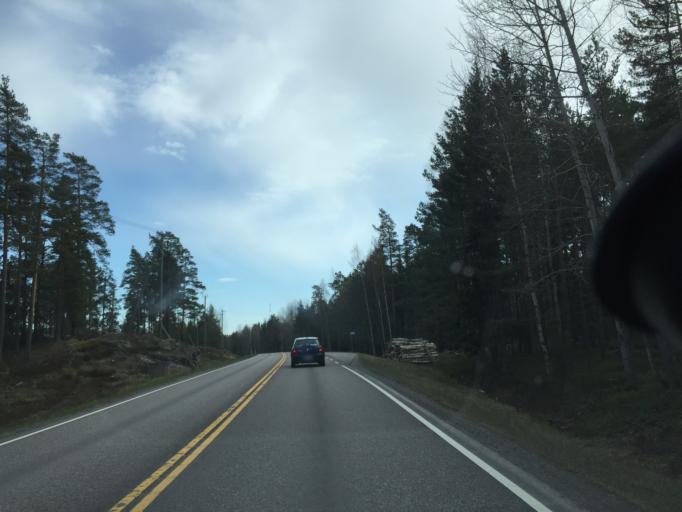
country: FI
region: Uusimaa
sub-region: Raaseporin
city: Ekenaes
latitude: 60.0281
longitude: 23.3698
